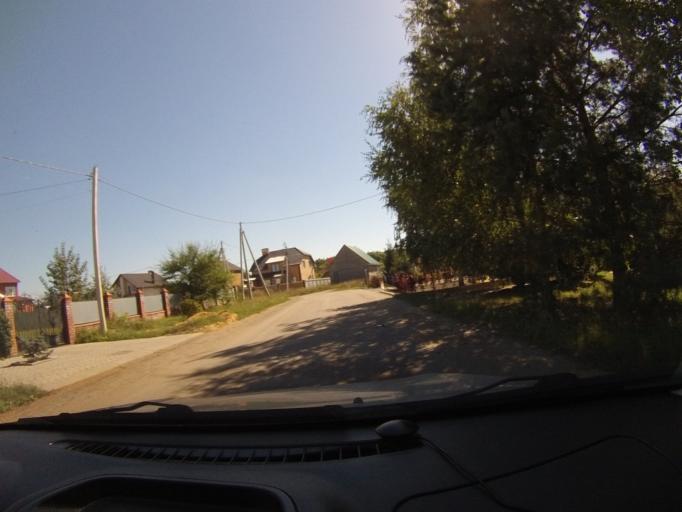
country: RU
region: Tambov
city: Komsomolets
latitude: 52.7618
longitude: 41.3625
